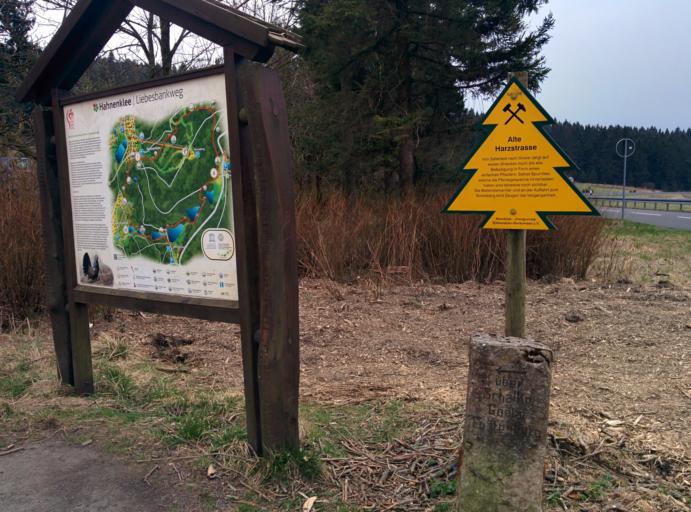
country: DE
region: Lower Saxony
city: Clausthal-Zellerfeld
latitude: 51.8544
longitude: 10.3648
